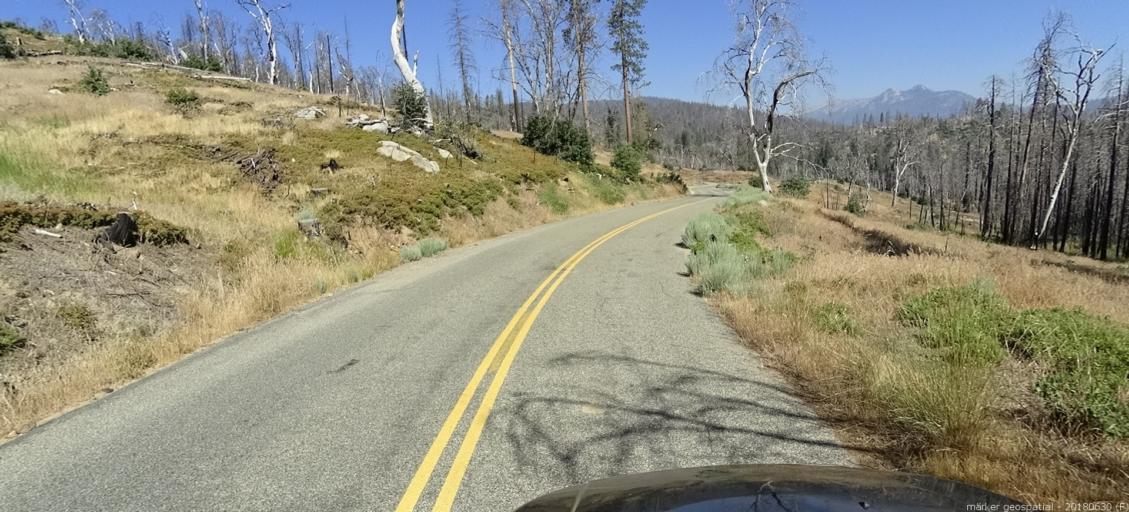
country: US
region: California
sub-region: Fresno County
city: Auberry
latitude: 37.2546
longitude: -119.3504
